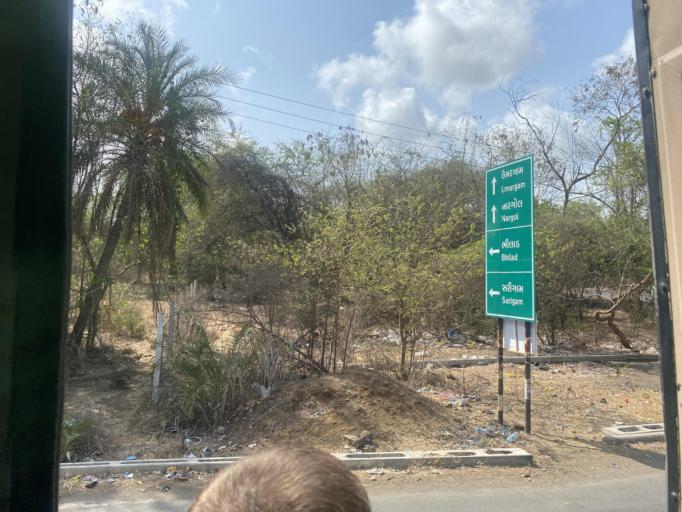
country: IN
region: Daman and Diu
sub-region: Daman District
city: Daman
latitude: 20.3366
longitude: 72.8022
